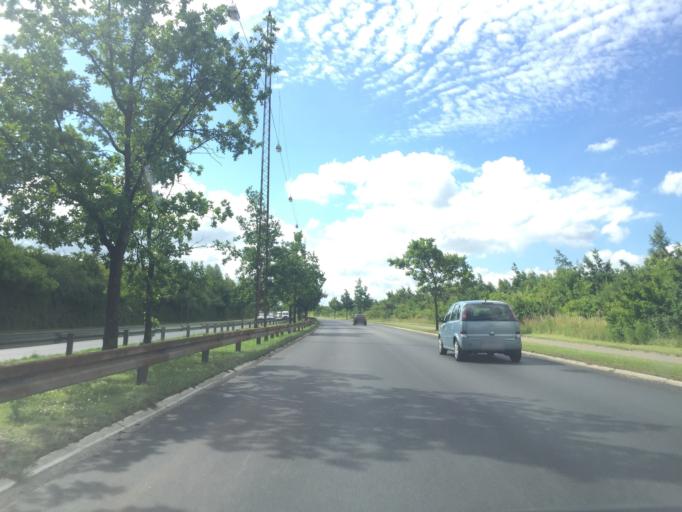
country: DK
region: Capital Region
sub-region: Hvidovre Kommune
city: Hvidovre
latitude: 55.6571
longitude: 12.4544
